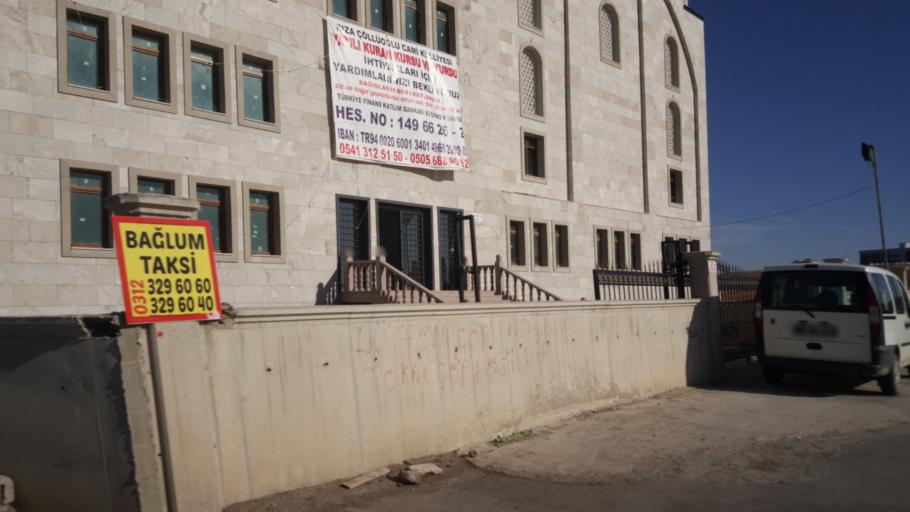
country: TR
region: Ankara
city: Mamak
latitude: 40.0313
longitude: 32.8643
